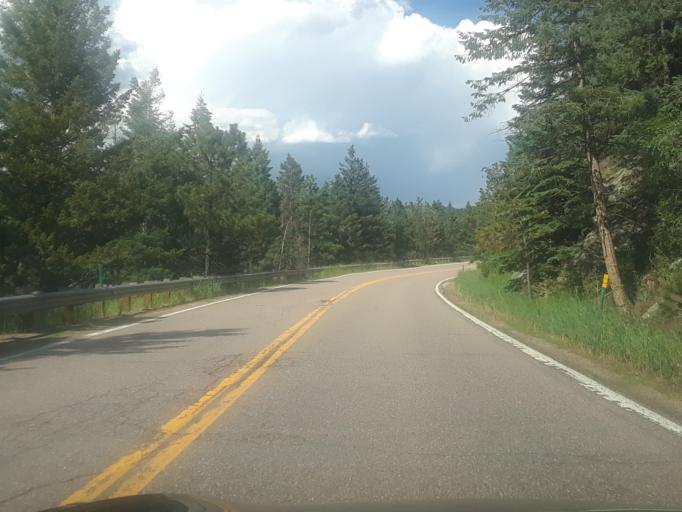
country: US
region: Colorado
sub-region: Jefferson County
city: Kittredge
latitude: 39.7177
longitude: -105.3593
